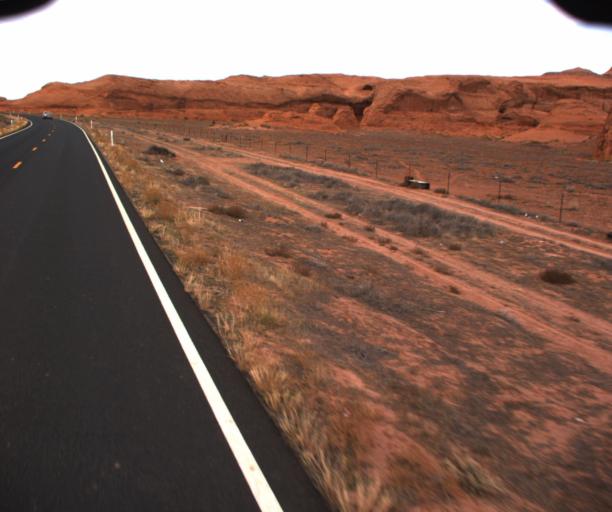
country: US
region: Arizona
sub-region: Apache County
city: Many Farms
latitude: 36.7639
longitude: -109.6520
